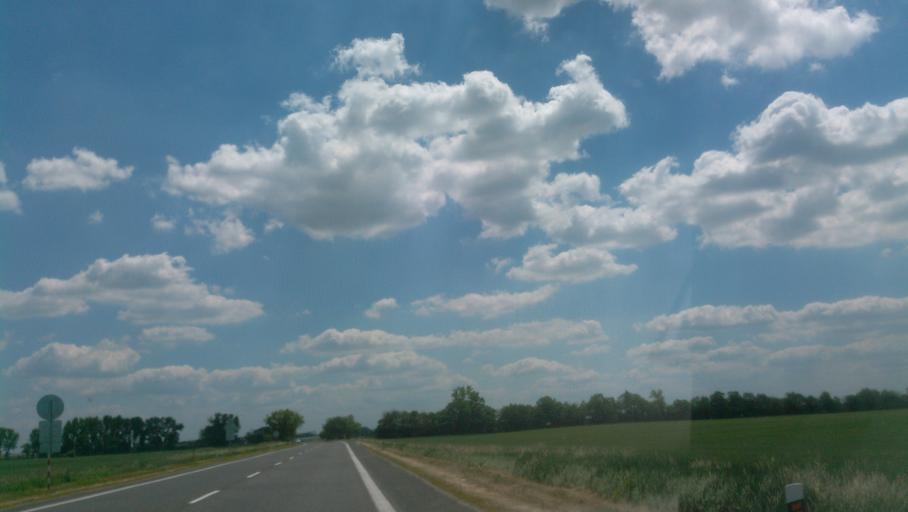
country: SK
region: Bratislavsky
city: Dunajska Luzna
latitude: 48.0611
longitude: 17.2824
